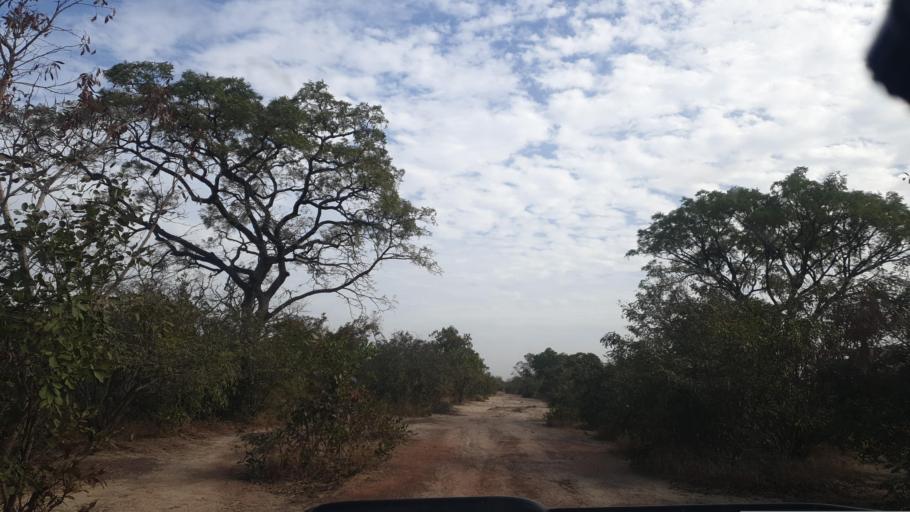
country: ML
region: Sikasso
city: Yanfolila
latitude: 11.4083
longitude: -8.0094
